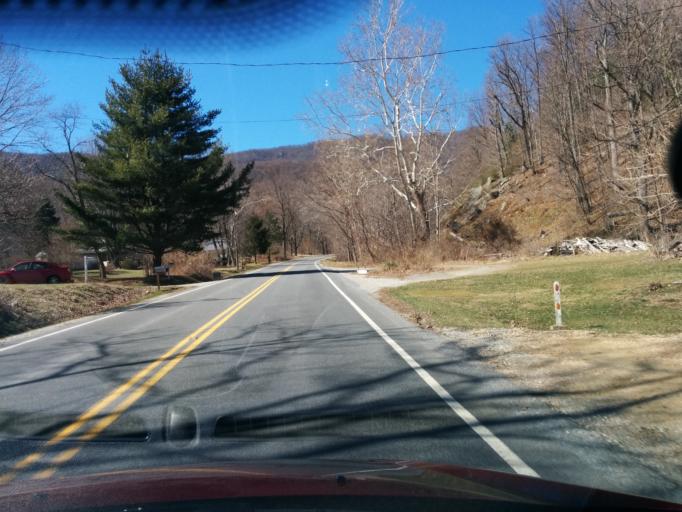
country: US
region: Virginia
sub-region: Nelson County
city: Nellysford
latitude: 37.8820
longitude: -78.9668
